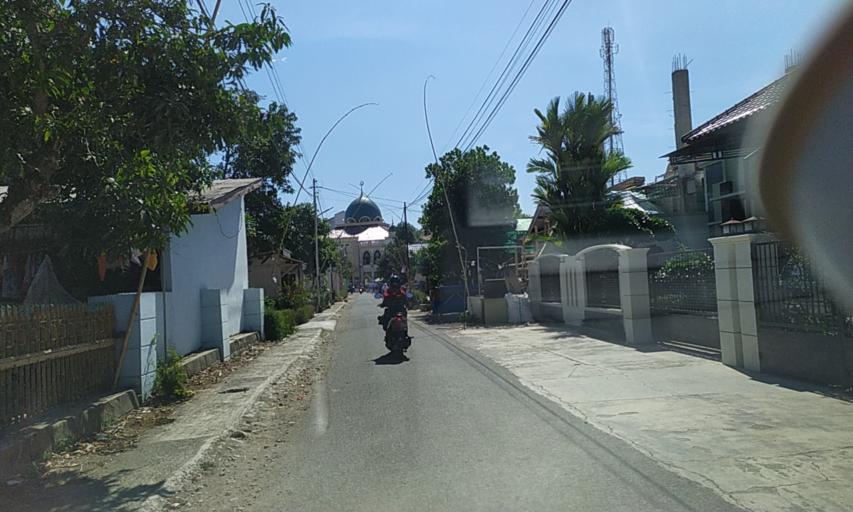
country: ID
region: Central Java
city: Kroya
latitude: -7.6301
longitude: 109.2481
